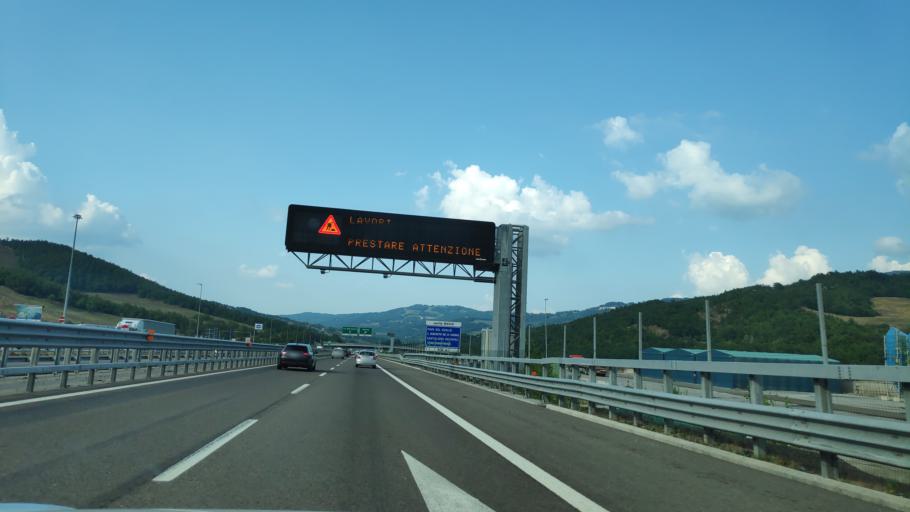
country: IT
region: Emilia-Romagna
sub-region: Provincia di Bologna
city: Castiglione dei Pepoli
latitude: 44.1496
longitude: 11.1940
